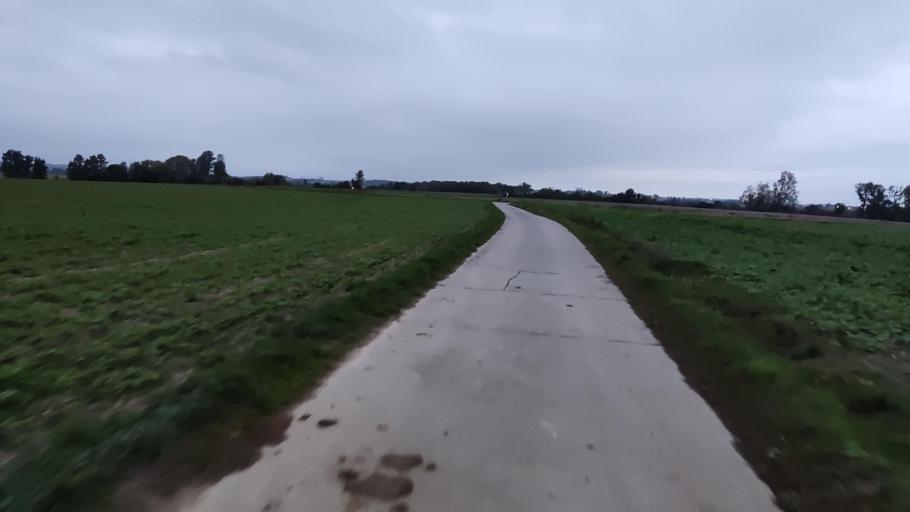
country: BE
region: Flanders
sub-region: Provincie Vlaams-Brabant
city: Tienen
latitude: 50.7742
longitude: 4.9284
